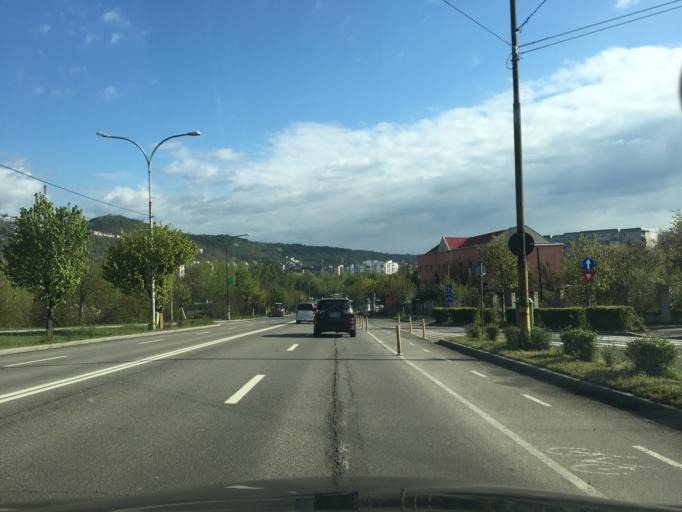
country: RO
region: Cluj
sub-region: Comuna Baciu
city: Baciu
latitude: 46.7582
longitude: 23.5428
